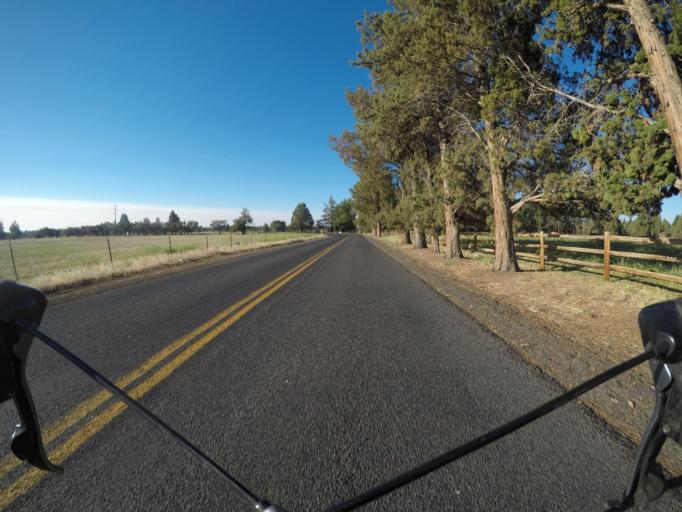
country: US
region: Oregon
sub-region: Deschutes County
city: Redmond
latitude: 44.2631
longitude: -121.2451
